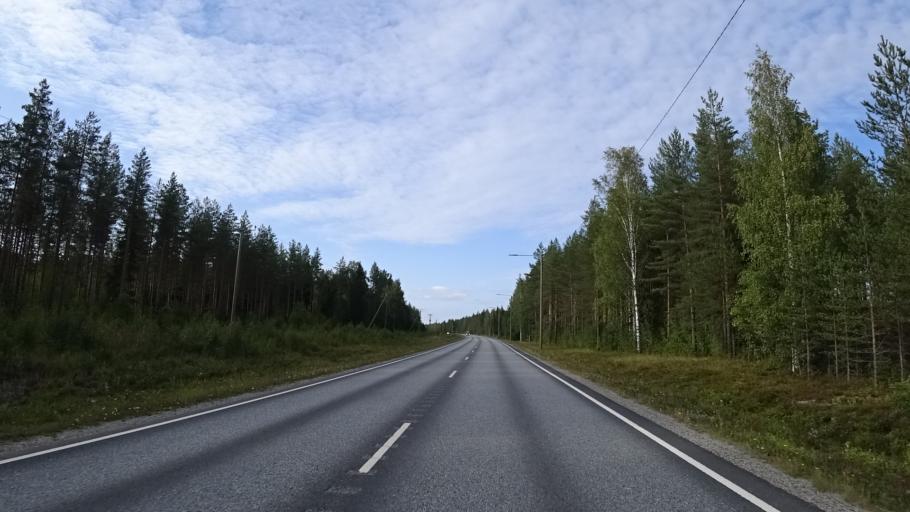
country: FI
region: North Karelia
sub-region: Joensuu
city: Eno
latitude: 62.8702
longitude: 30.2019
